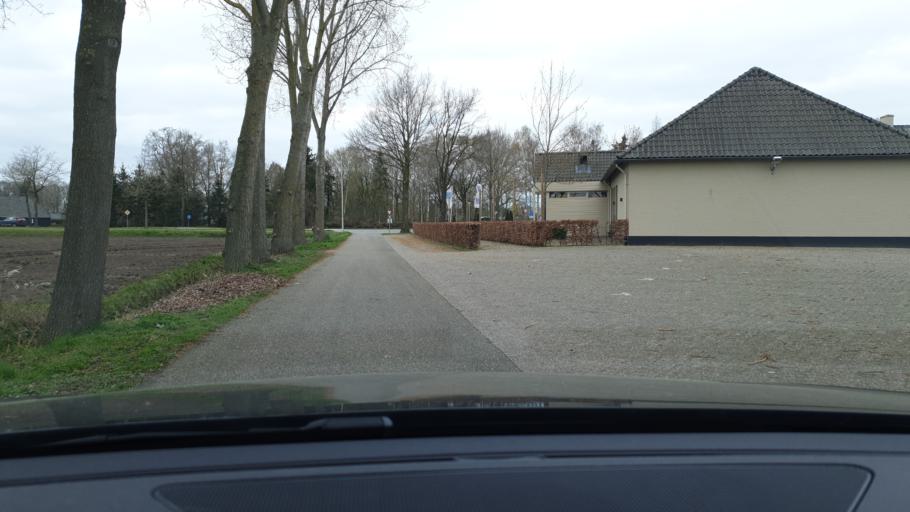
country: NL
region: North Brabant
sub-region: Gemeente Oirschot
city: Oirschot
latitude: 51.5047
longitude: 5.3414
